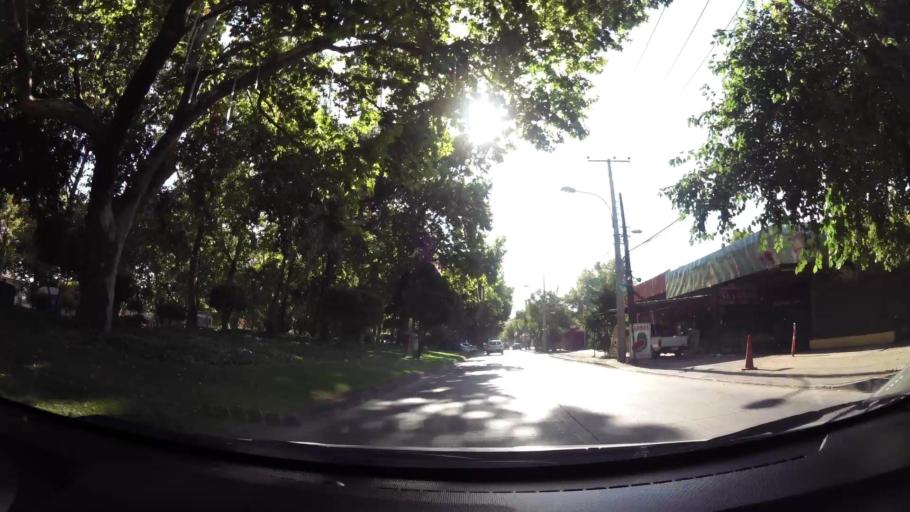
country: CL
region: Maule
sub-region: Provincia de Talca
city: Talca
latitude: -35.4226
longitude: -71.6516
